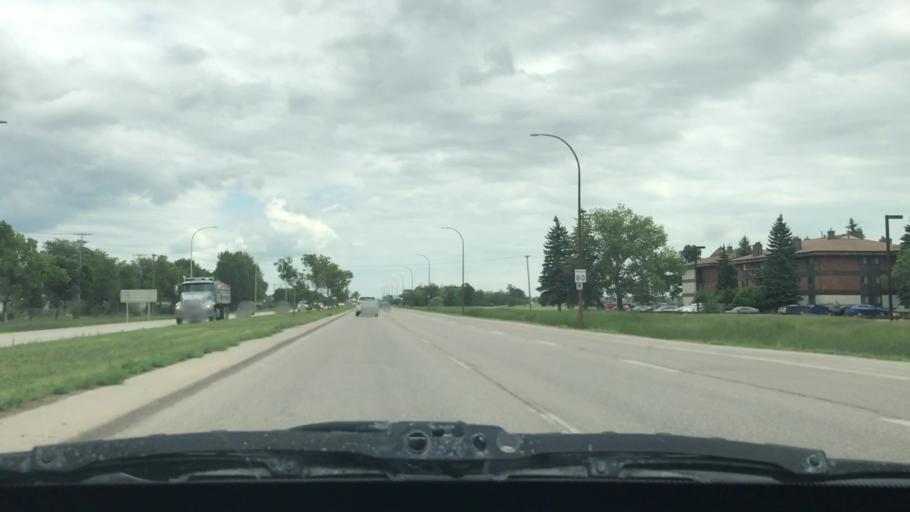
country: CA
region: Manitoba
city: Winnipeg
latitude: 49.8559
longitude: -97.0633
